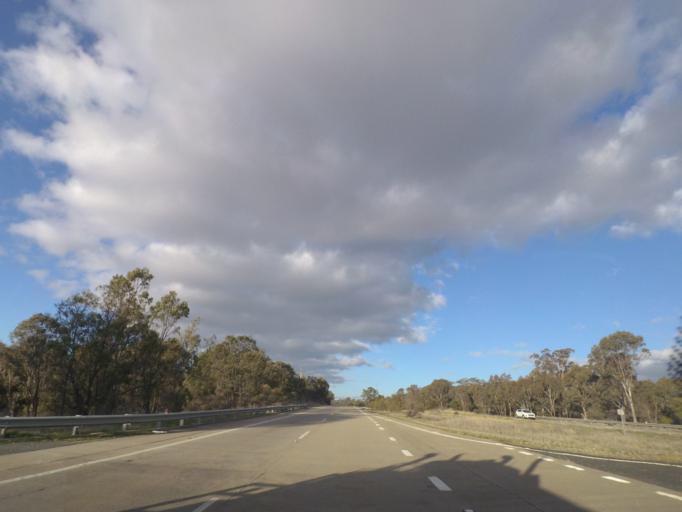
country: AU
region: New South Wales
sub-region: Yass Valley
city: Yass
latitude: -34.8002
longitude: 148.5220
